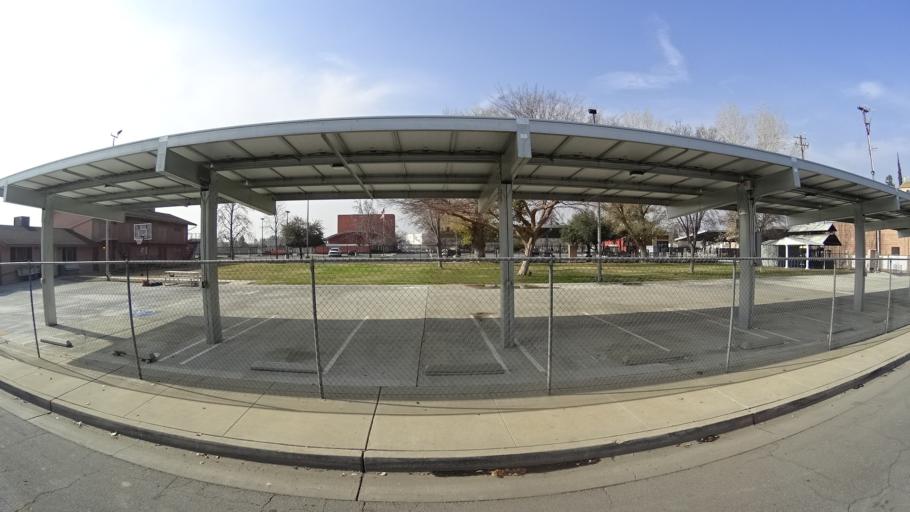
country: US
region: California
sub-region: Kern County
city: Bakersfield
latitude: 35.3723
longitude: -119.0060
